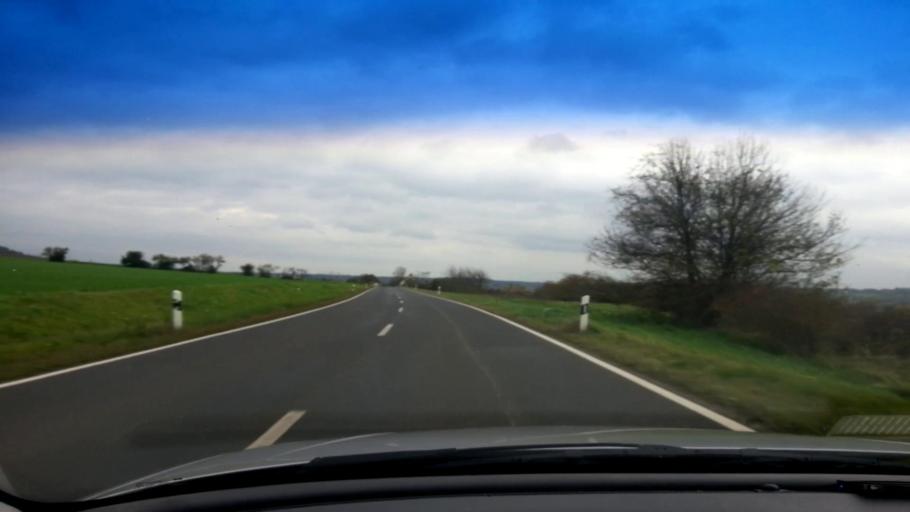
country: DE
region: Bavaria
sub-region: Regierungsbezirk Unterfranken
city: Stettfeld
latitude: 49.9546
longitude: 10.7390
